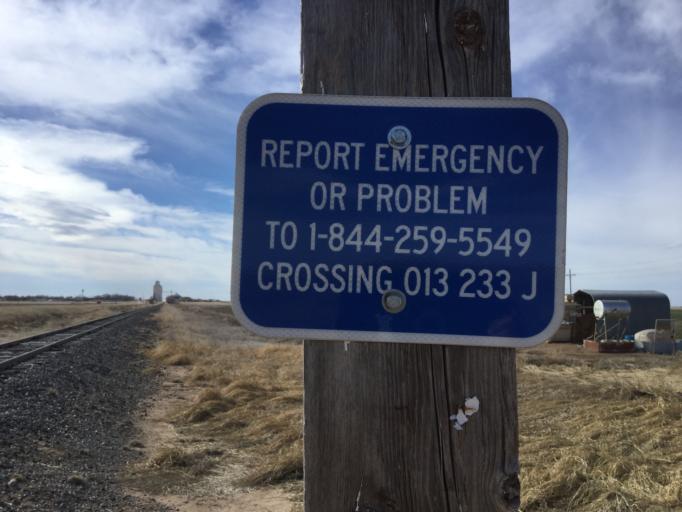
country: US
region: Kansas
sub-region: Stevens County
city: Hugoton
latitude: 37.1268
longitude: -101.6098
